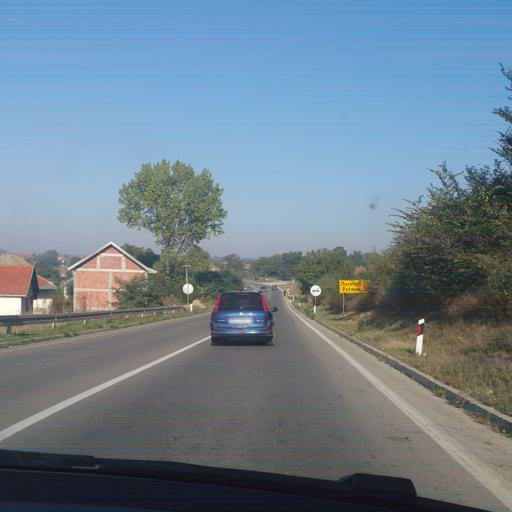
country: RS
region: Central Serbia
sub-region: Toplicki Okrug
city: Prokuplje
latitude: 43.2385
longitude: 21.4962
